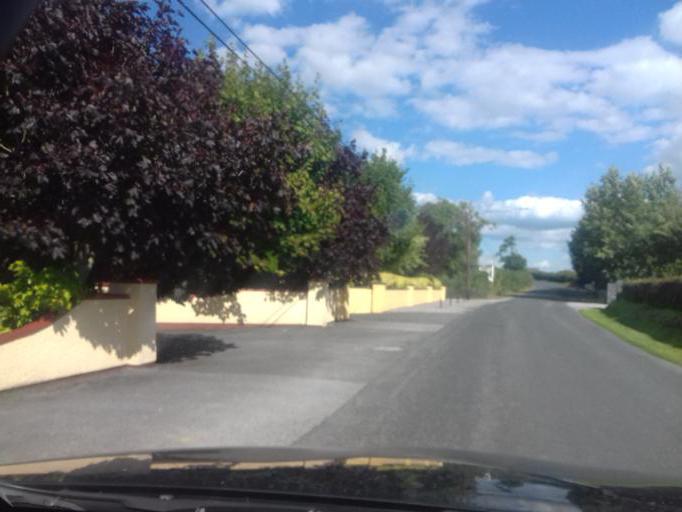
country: IE
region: Leinster
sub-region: Kilkenny
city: Thomastown
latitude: 52.5380
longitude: -7.2411
